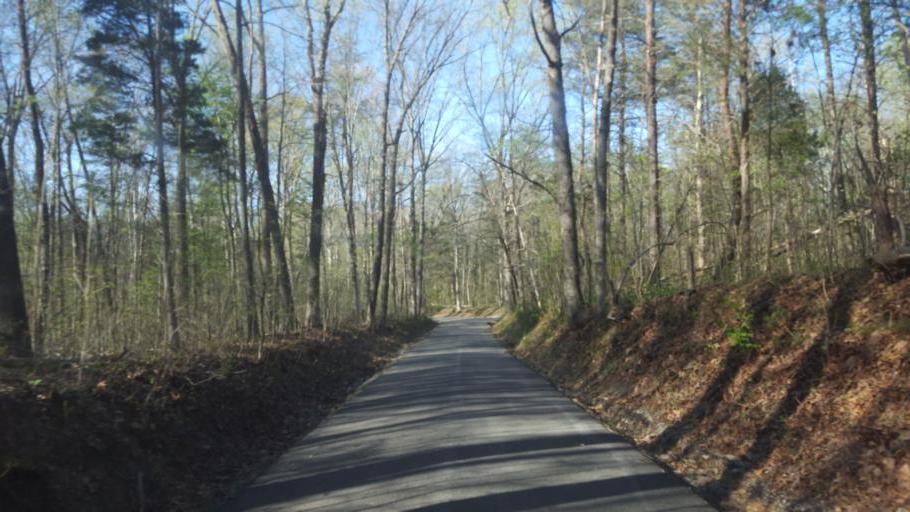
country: US
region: Kentucky
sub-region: Barren County
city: Cave City
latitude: 37.1856
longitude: -86.0482
